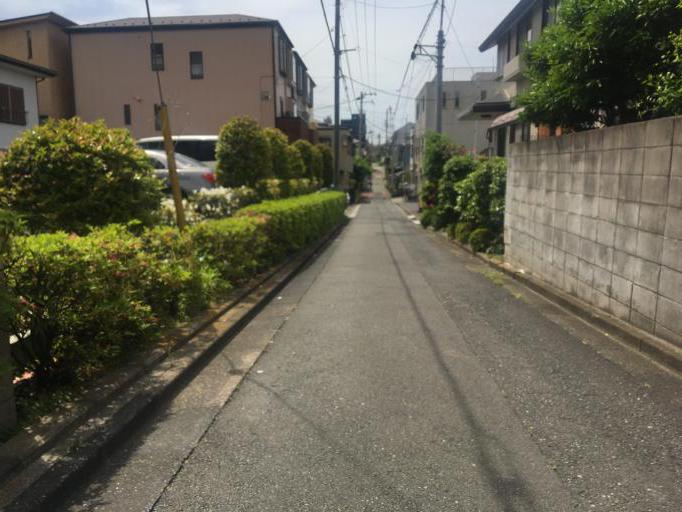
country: JP
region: Saitama
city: Yono
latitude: 35.8676
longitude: 139.6436
